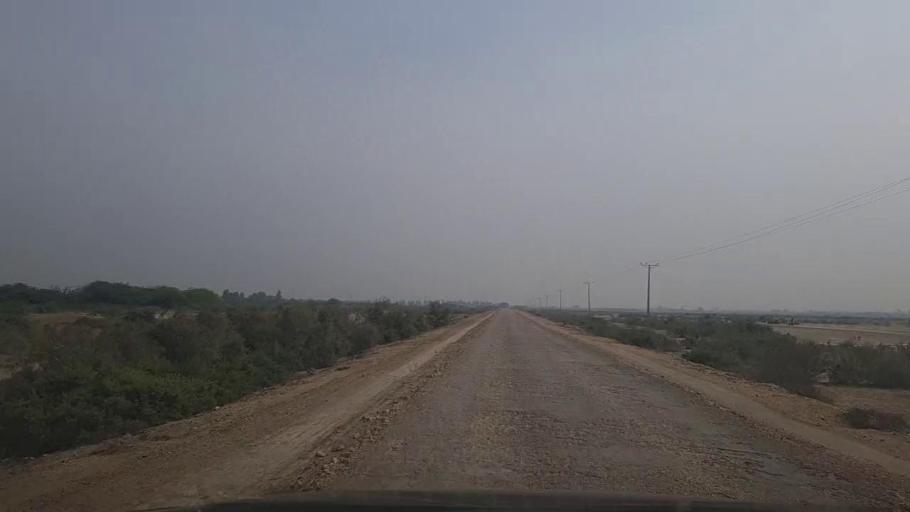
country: PK
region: Sindh
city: Mirpur Sakro
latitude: 24.4592
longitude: 67.6972
